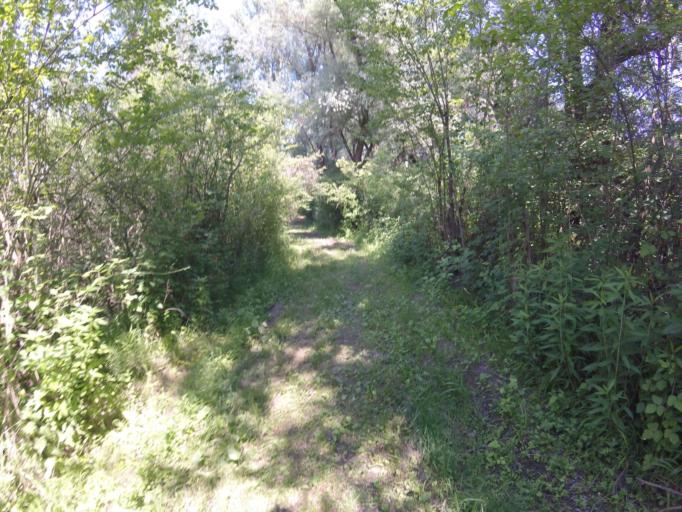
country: HR
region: Osjecko-Baranjska
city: Viljevo
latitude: 45.8000
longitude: 18.0881
